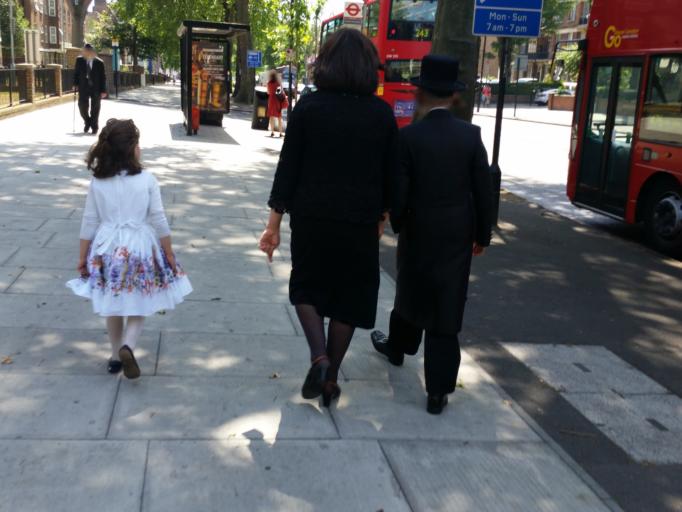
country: GB
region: England
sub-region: Greater London
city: Harringay
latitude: 51.5701
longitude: -0.0727
